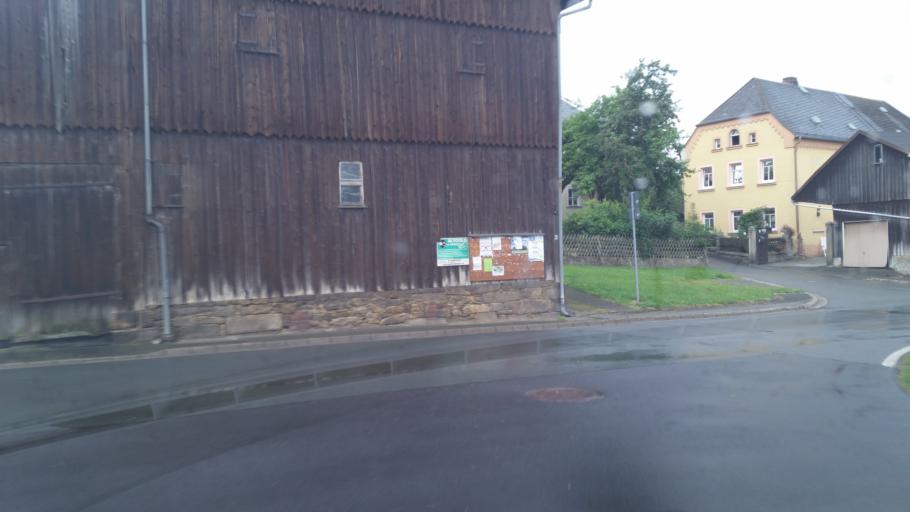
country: DE
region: Bavaria
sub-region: Upper Franconia
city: Rehau
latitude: 50.2232
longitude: 12.0289
